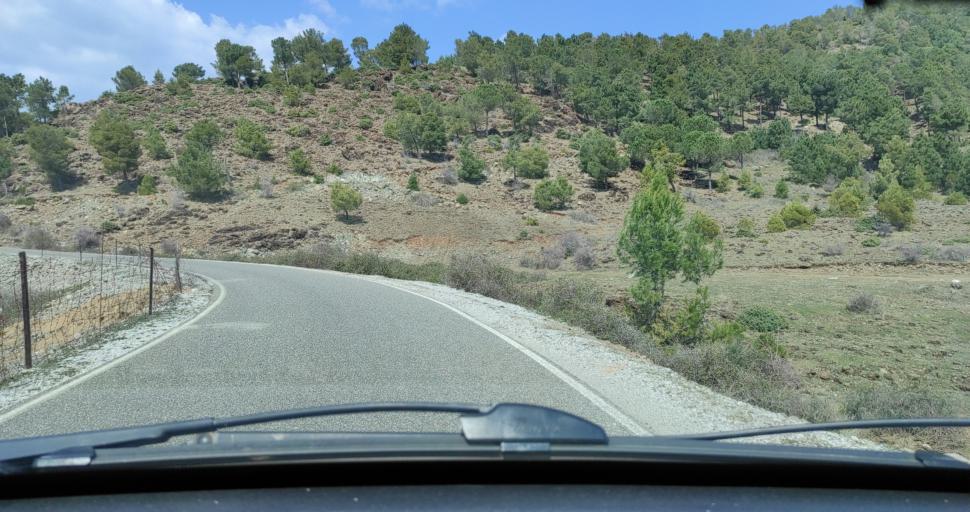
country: AL
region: Shkoder
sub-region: Rrethi i Shkodres
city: Vau i Dejes
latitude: 41.9888
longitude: 19.6455
